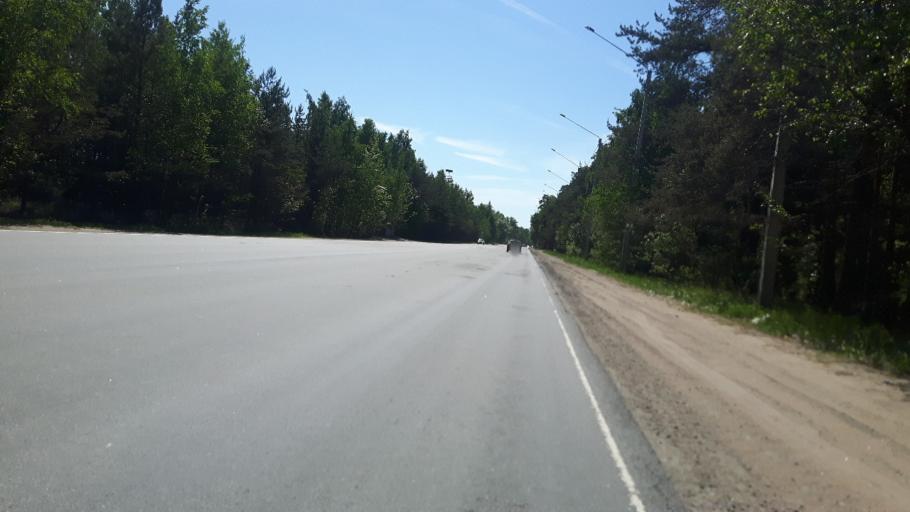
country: RU
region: Leningrad
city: Sosnovyy Bor
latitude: 59.8714
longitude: 29.0822
